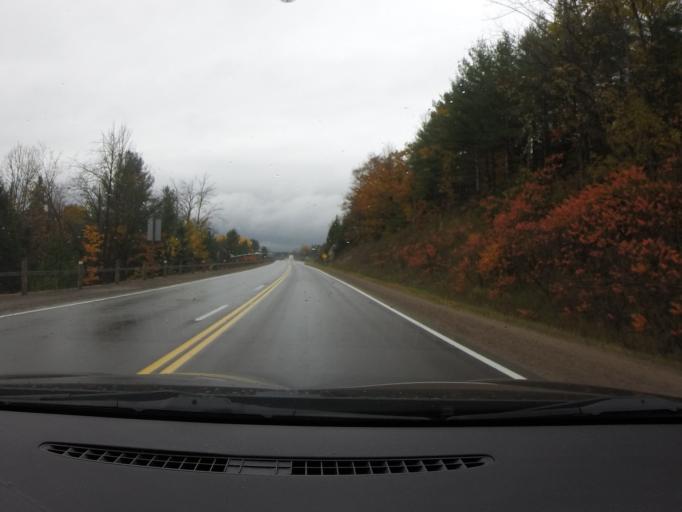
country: CA
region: Ontario
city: Belleville
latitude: 44.5572
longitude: -77.3112
